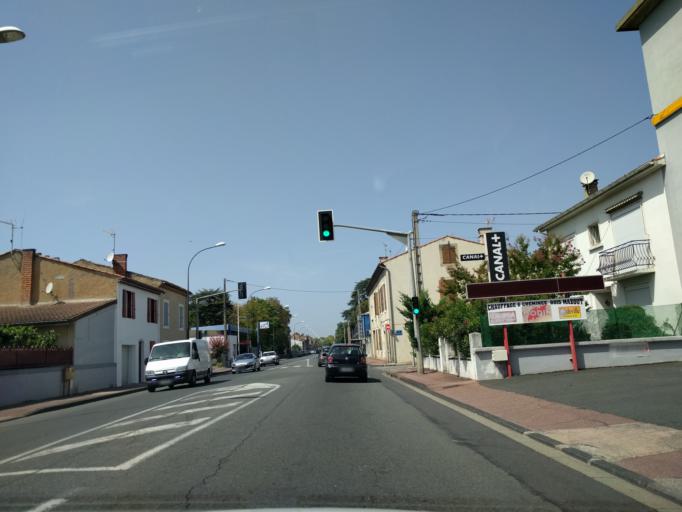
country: FR
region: Midi-Pyrenees
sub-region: Departement du Tarn
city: Castres
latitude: 43.5984
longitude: 2.2584
